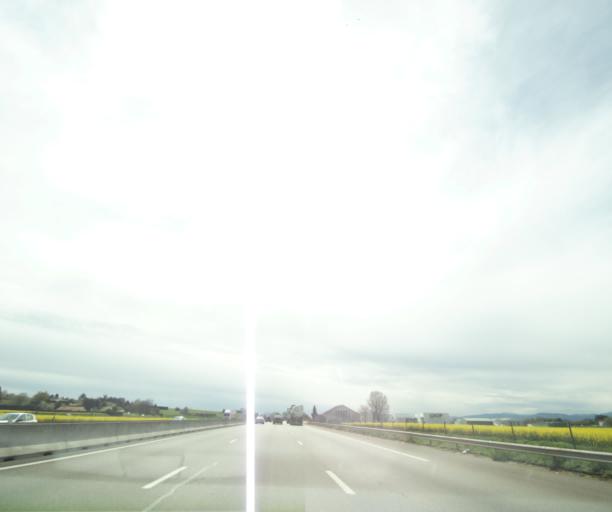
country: FR
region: Rhone-Alpes
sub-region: Departement de l'Isere
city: Reventin-Vaugris
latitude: 45.4679
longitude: 4.8330
